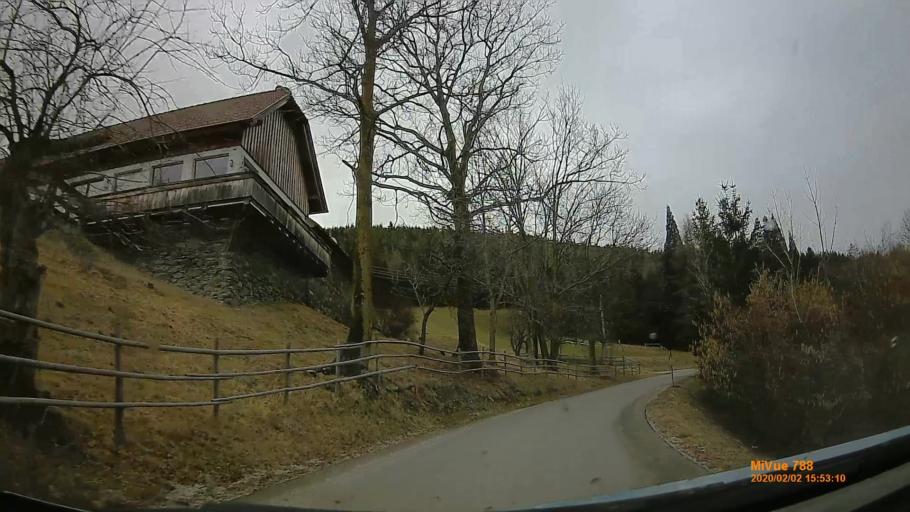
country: AT
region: Lower Austria
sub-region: Politischer Bezirk Neunkirchen
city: Reichenau an der Rax
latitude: 47.6750
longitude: 15.7996
